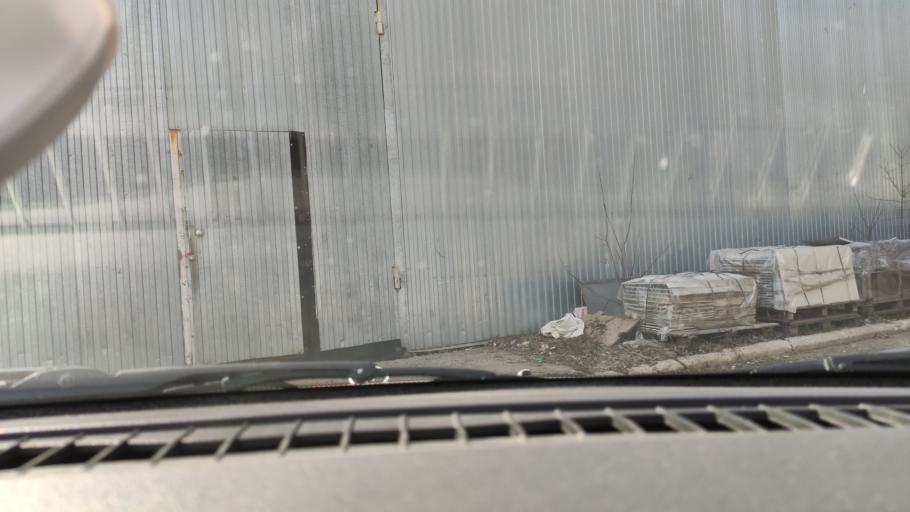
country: RU
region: Samara
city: Samara
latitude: 53.2706
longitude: 50.1887
